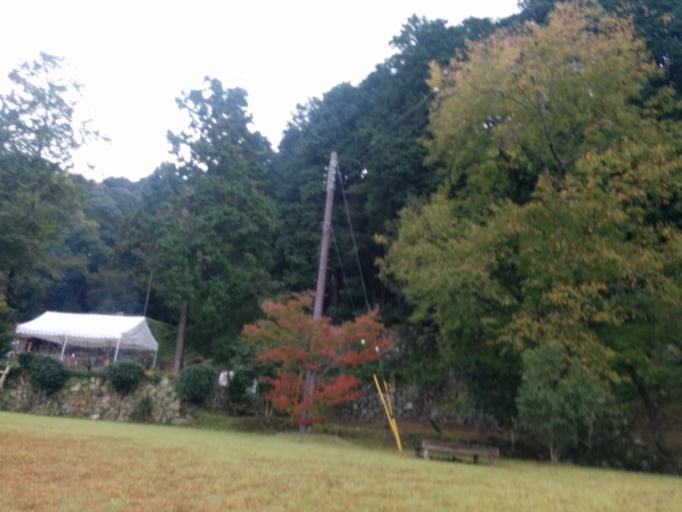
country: JP
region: Shiga Prefecture
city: Omihachiman
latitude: 35.1531
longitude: 136.1394
